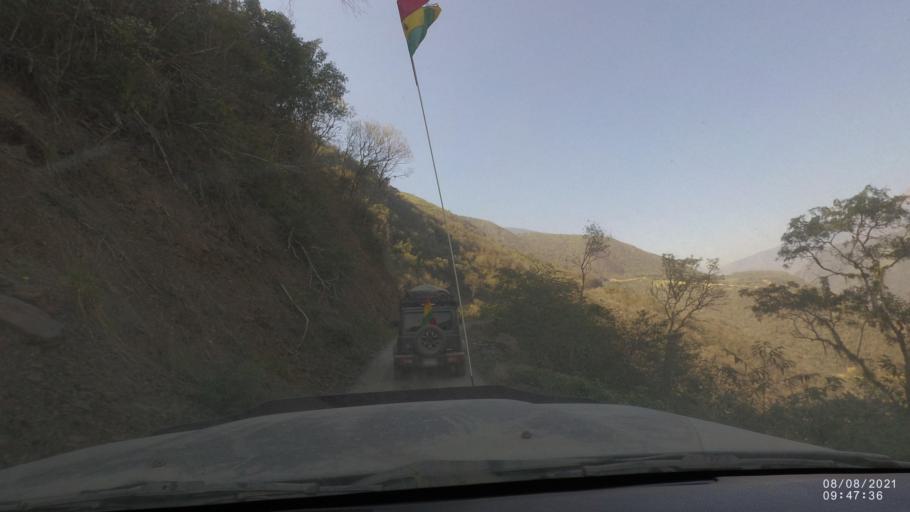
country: BO
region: La Paz
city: Quime
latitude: -16.6098
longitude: -66.7294
